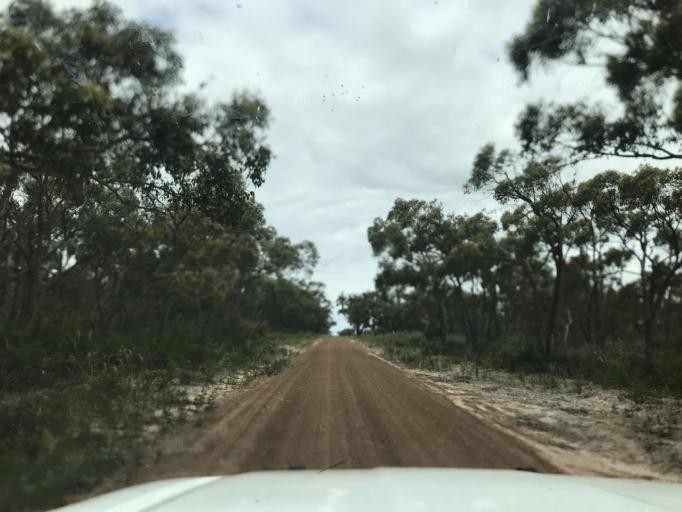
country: AU
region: South Australia
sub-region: Naracoorte and Lucindale
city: Naracoorte
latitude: -36.9222
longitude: 141.3266
